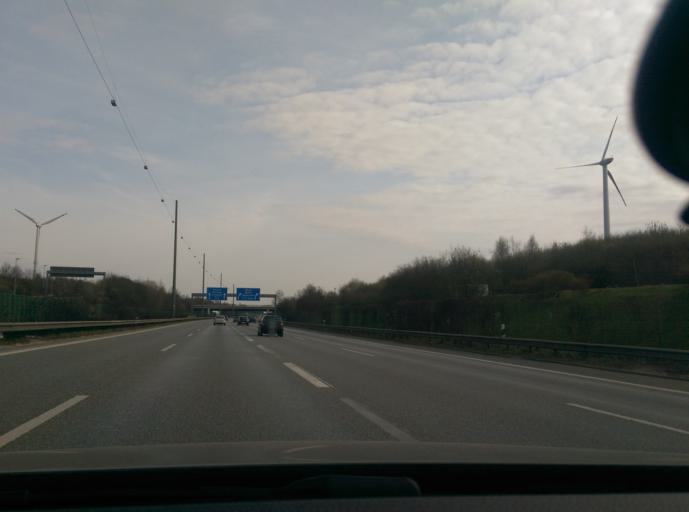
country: DE
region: Hamburg
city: Rothenburgsort
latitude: 53.5122
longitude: 10.0333
